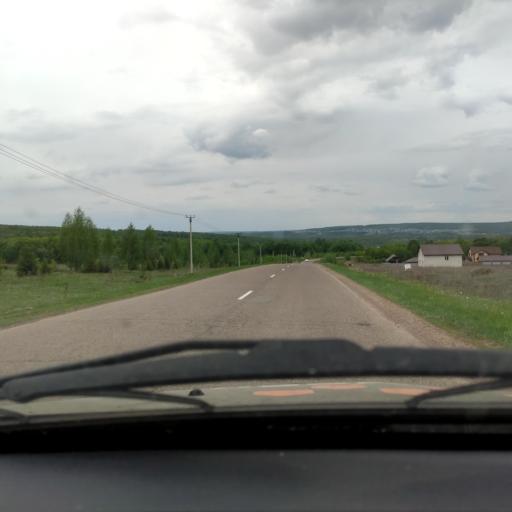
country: RU
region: Bashkortostan
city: Avdon
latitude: 54.5822
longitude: 55.7258
